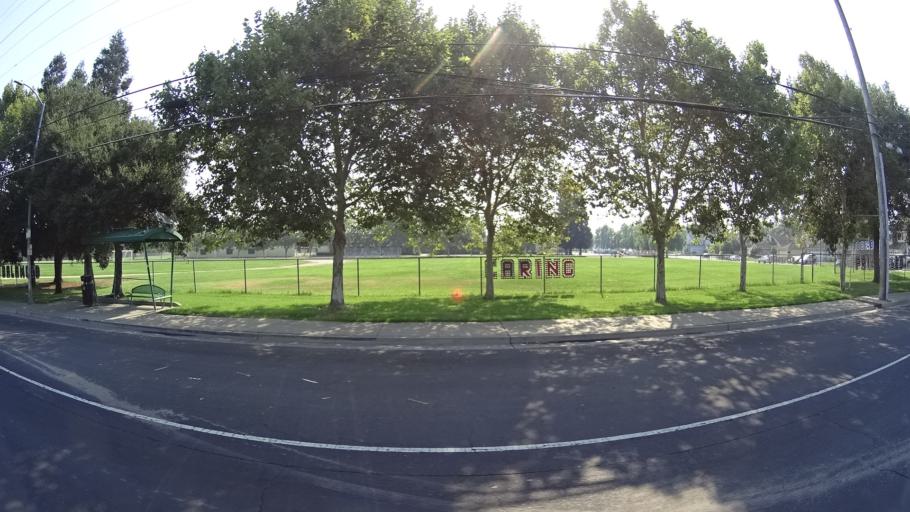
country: US
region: California
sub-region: Sacramento County
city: Laguna
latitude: 38.4193
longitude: -121.4178
